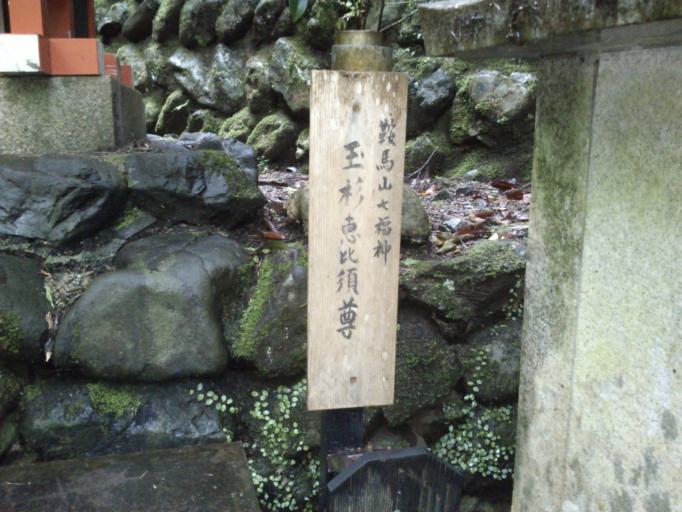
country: JP
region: Kyoto
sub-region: Kyoto-shi
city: Kamigyo-ku
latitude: 35.1163
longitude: 135.7717
